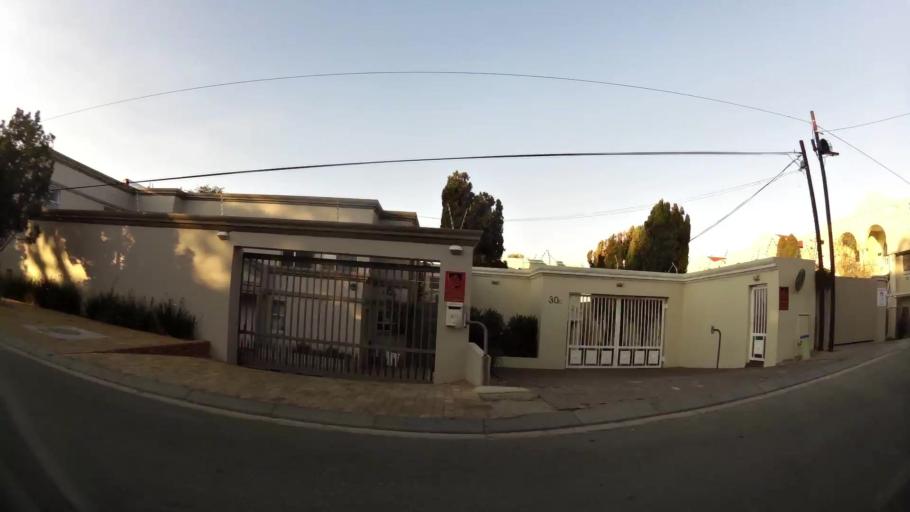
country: ZA
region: Gauteng
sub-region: City of Johannesburg Metropolitan Municipality
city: Modderfontein
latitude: -26.0721
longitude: 28.0616
